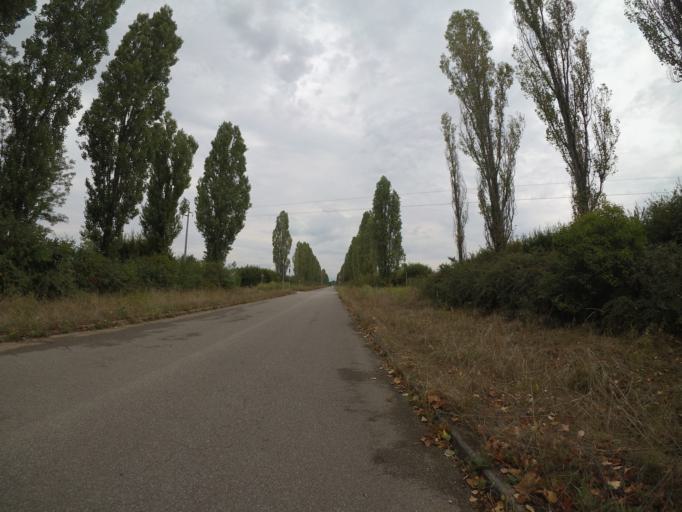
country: IT
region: Friuli Venezia Giulia
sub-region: Provincia di Udine
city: Codroipo
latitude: 45.9604
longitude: 13.0111
